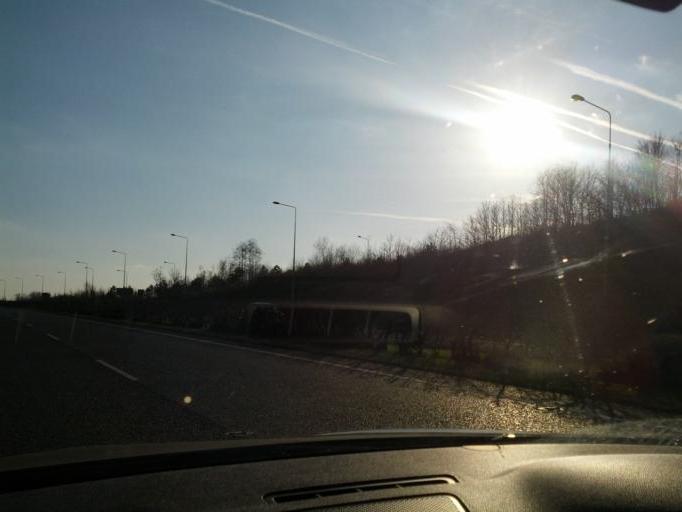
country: IE
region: Leinster
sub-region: Laois
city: Portlaoise
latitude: 53.0499
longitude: -7.2394
